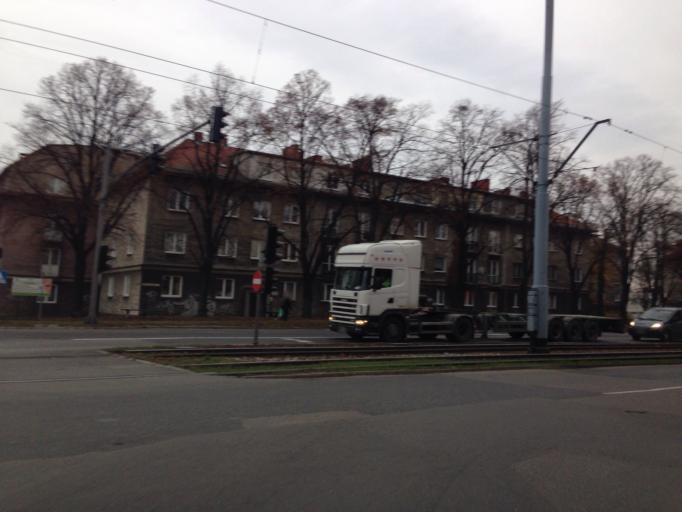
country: PL
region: Pomeranian Voivodeship
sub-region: Gdansk
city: Gdansk
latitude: 54.3878
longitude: 18.6221
